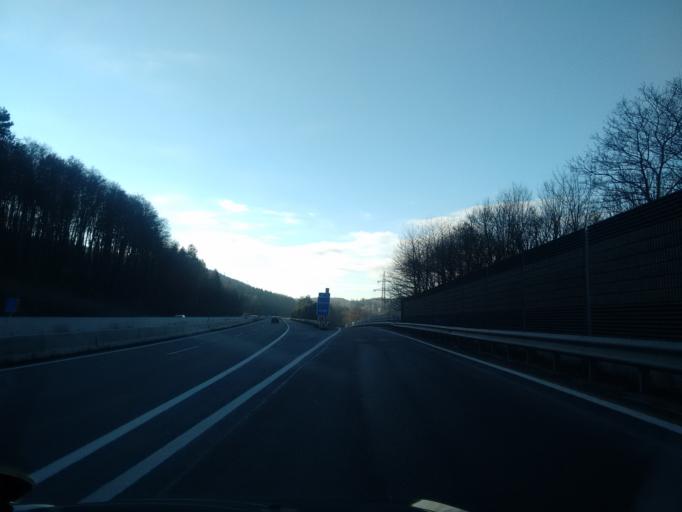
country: AT
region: Lower Austria
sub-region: Politischer Bezirk Wien-Umgebung
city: Pressbaum
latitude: 48.1761
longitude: 16.0660
